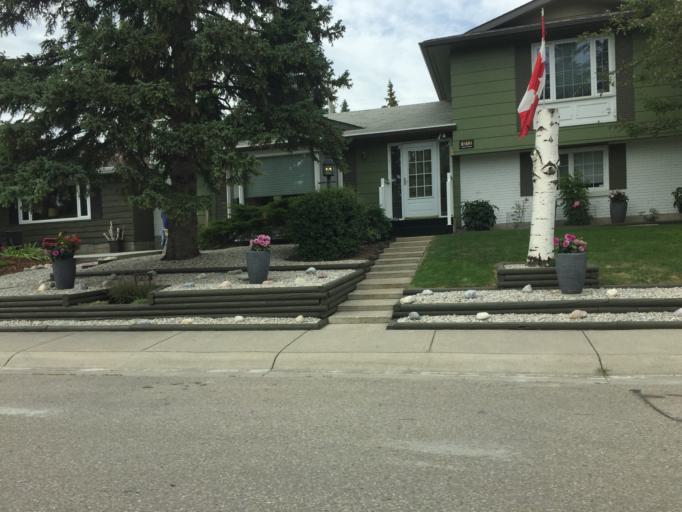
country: CA
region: Alberta
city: Calgary
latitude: 50.9367
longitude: -114.0388
